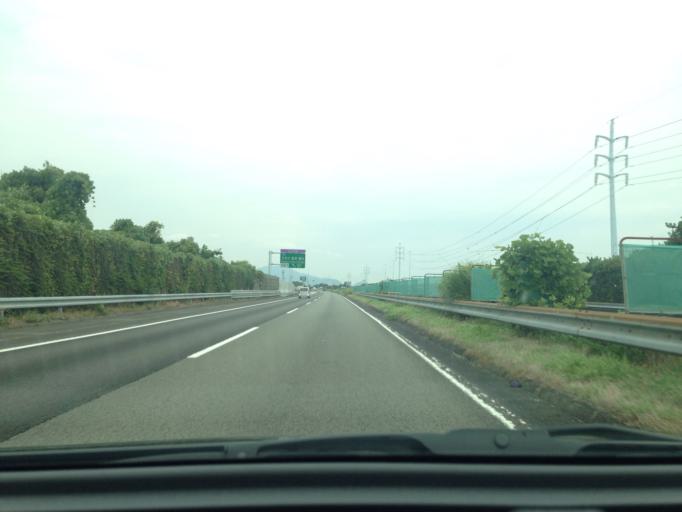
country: JP
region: Shizuoka
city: Fujieda
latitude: 34.8163
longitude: 138.2640
